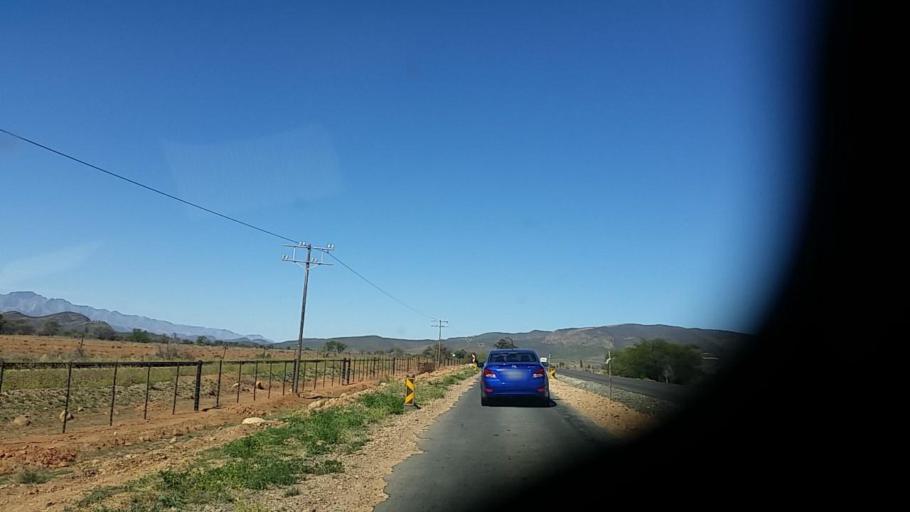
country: ZA
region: Western Cape
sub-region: Eden District Municipality
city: Oudtshoorn
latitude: -33.5614
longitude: 22.4027
